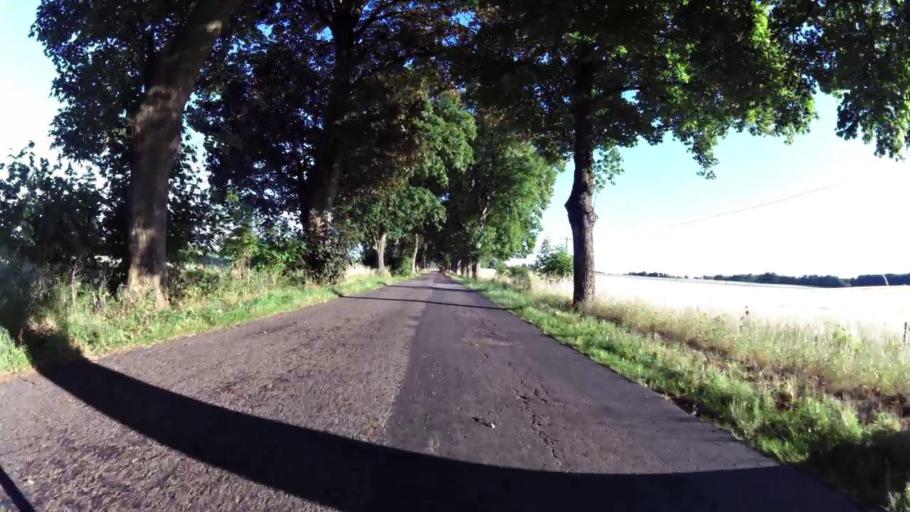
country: PL
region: West Pomeranian Voivodeship
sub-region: Powiat swidwinski
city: Swidwin
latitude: 53.7505
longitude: 15.6898
